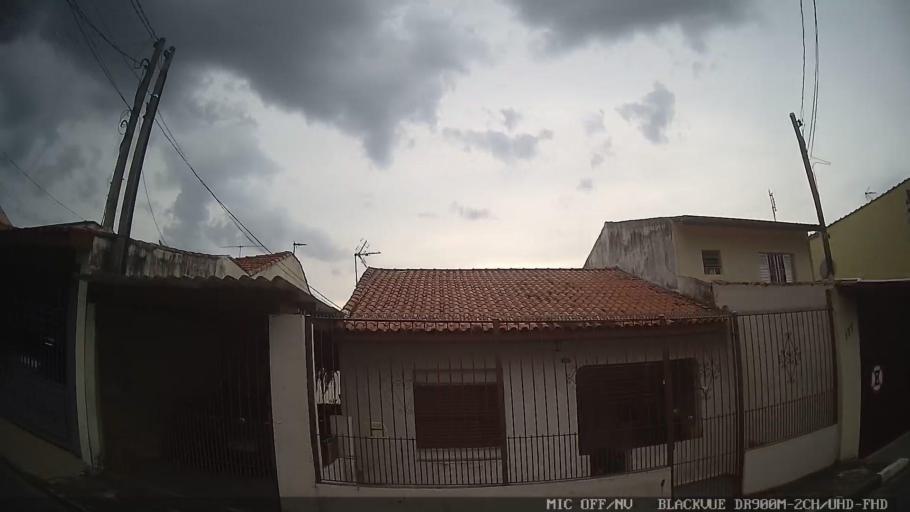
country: BR
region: Sao Paulo
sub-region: Atibaia
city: Atibaia
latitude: -23.1129
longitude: -46.5608
